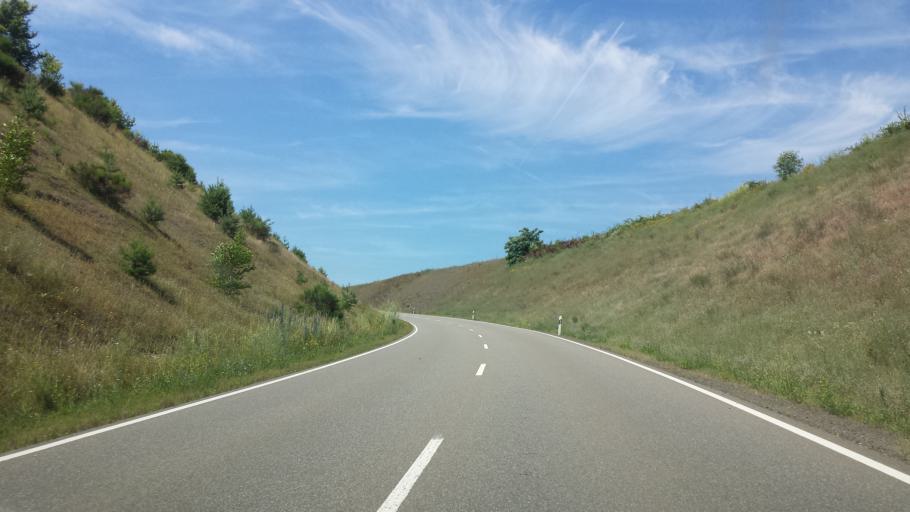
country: DE
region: Rheinland-Pfalz
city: Eisenberg
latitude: 49.5667
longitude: 8.0749
